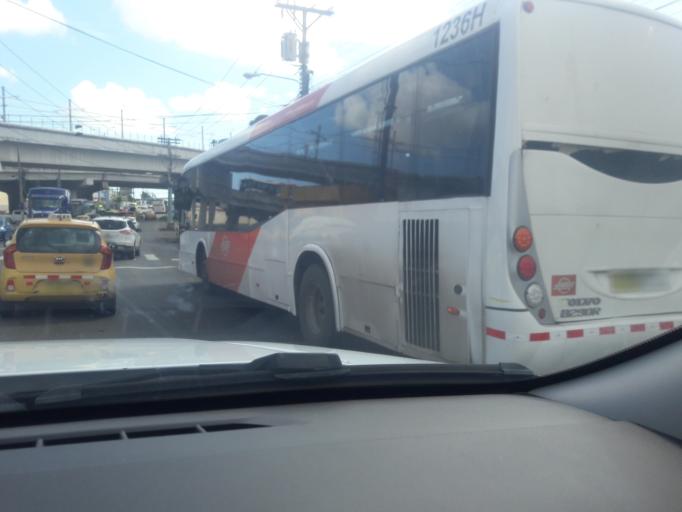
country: PA
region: Panama
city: San Miguelito
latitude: 9.0592
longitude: -79.4324
